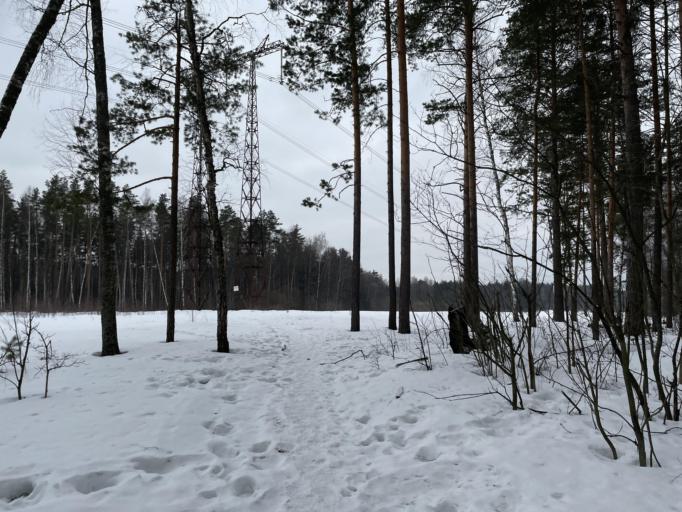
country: RU
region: Vladimir
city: Pokrov
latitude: 55.9435
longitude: 39.2403
